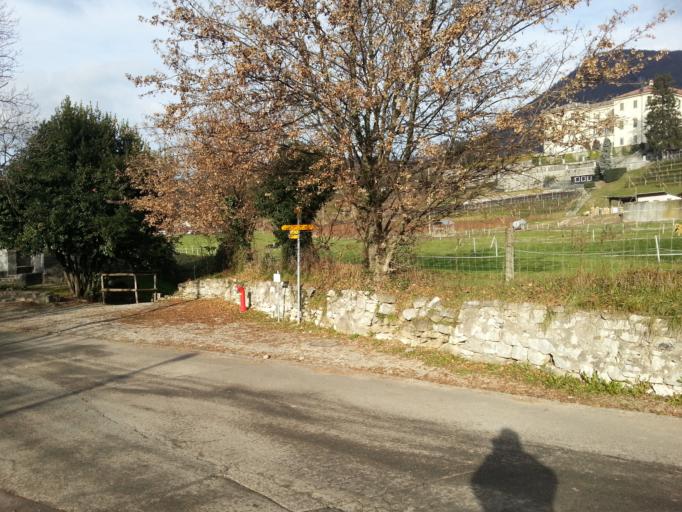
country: CH
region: Ticino
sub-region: Mendrisio District
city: Castel San Pietro
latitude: 45.8600
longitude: 9.0028
